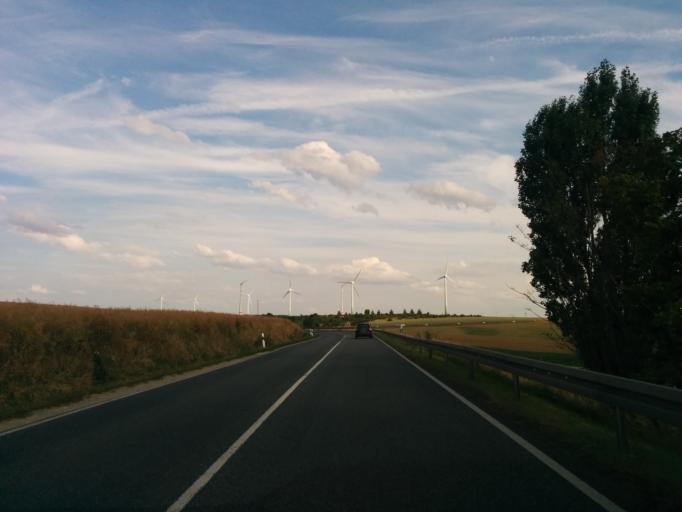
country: DE
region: Thuringia
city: Kleinfurra
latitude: 51.4461
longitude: 10.7836
